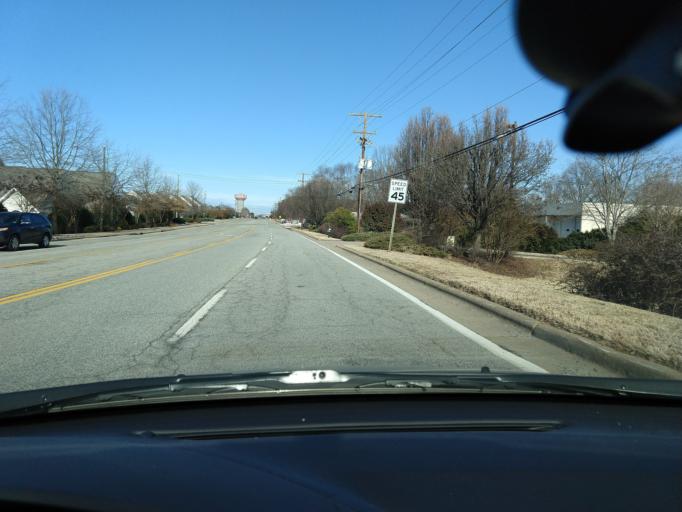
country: US
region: North Carolina
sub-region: Guilford County
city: Oak Ridge
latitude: 36.1134
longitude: -79.9540
